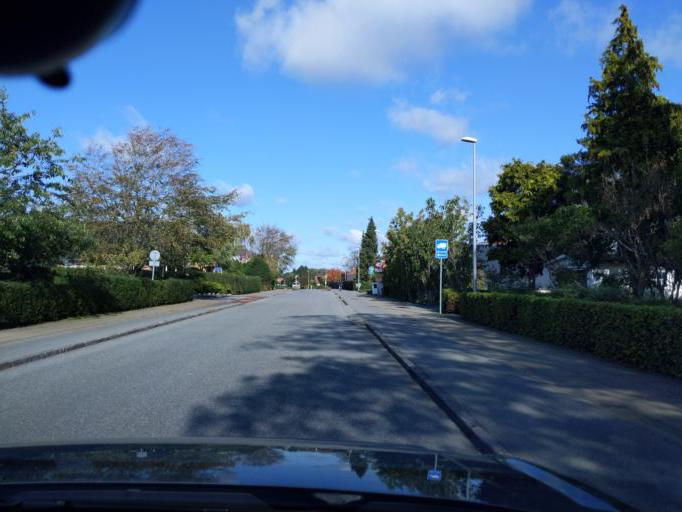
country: DK
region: Central Jutland
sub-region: Viborg Kommune
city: Viborg
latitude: 56.4653
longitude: 9.4230
